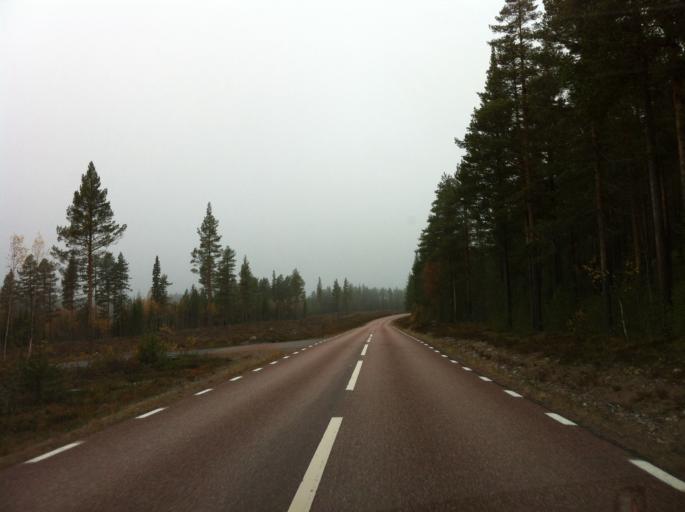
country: NO
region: Hedmark
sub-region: Trysil
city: Innbygda
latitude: 61.7757
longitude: 12.9460
